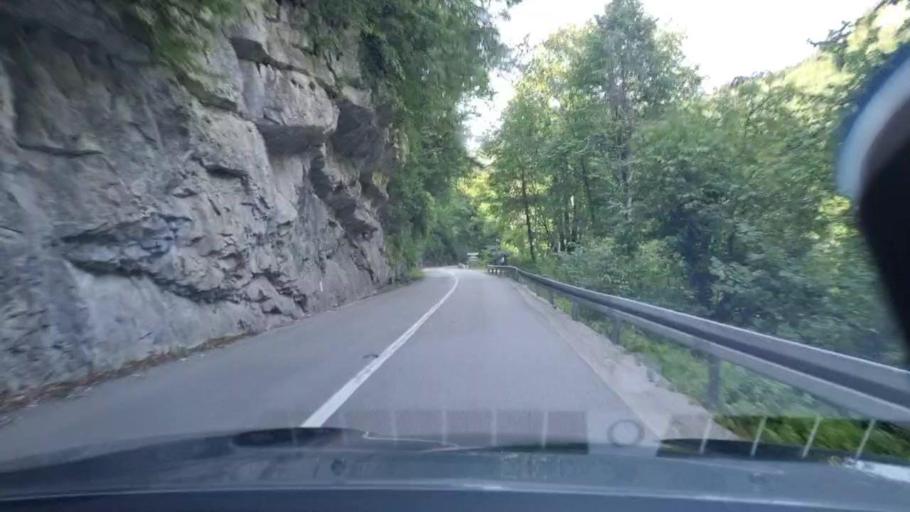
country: BA
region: Federation of Bosnia and Herzegovina
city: Bosanska Krupa
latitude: 44.8661
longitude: 16.0897
